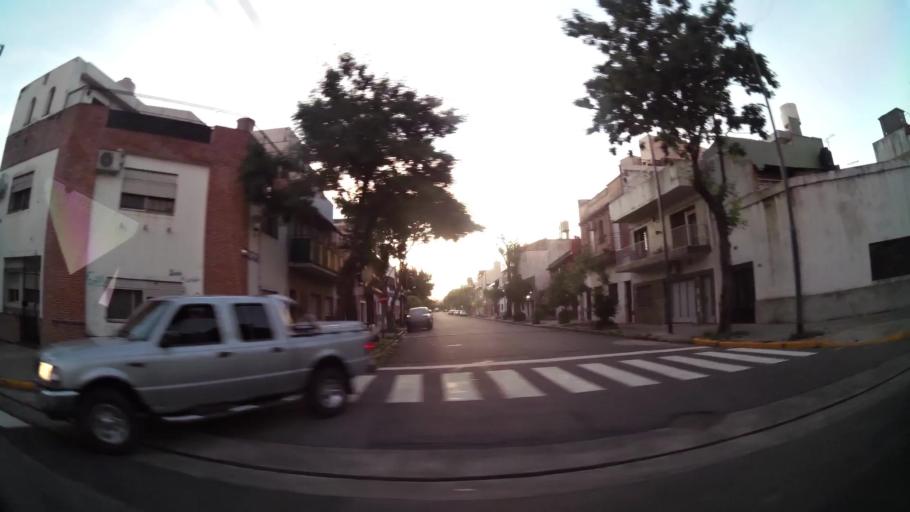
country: AR
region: Buenos Aires F.D.
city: Villa Santa Rita
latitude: -34.6377
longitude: -58.4364
